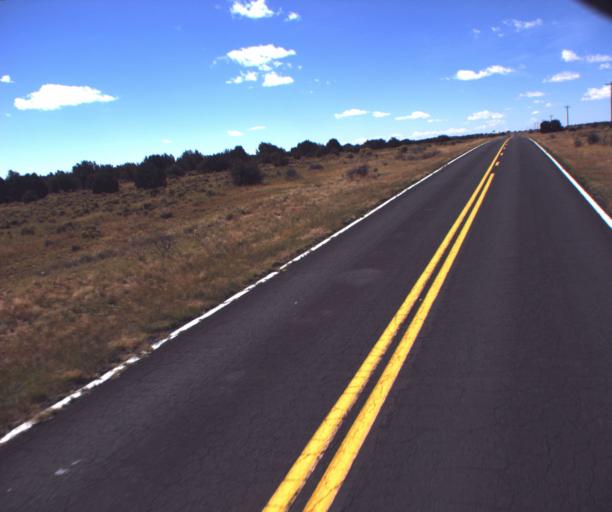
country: US
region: New Mexico
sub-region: McKinley County
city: Zuni Pueblo
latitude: 34.9695
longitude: -109.1440
